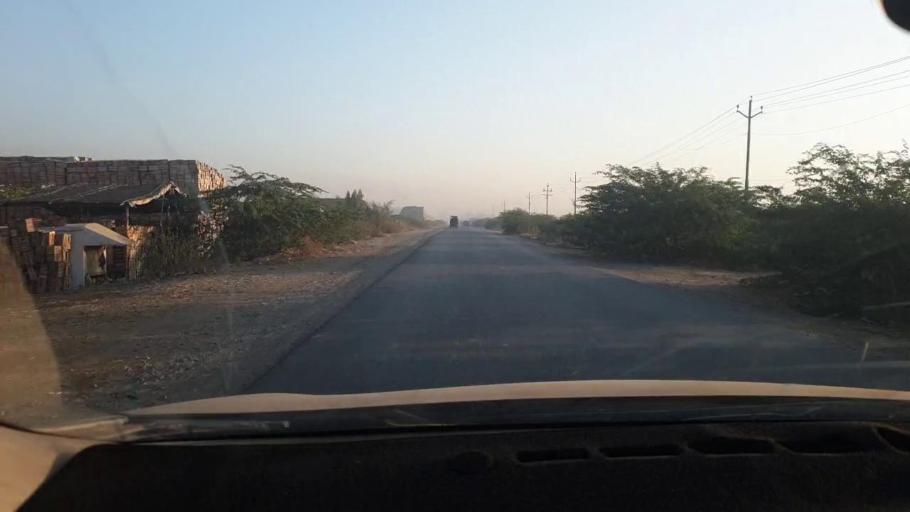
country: PK
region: Sindh
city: Malir Cantonment
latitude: 24.9991
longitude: 67.1459
